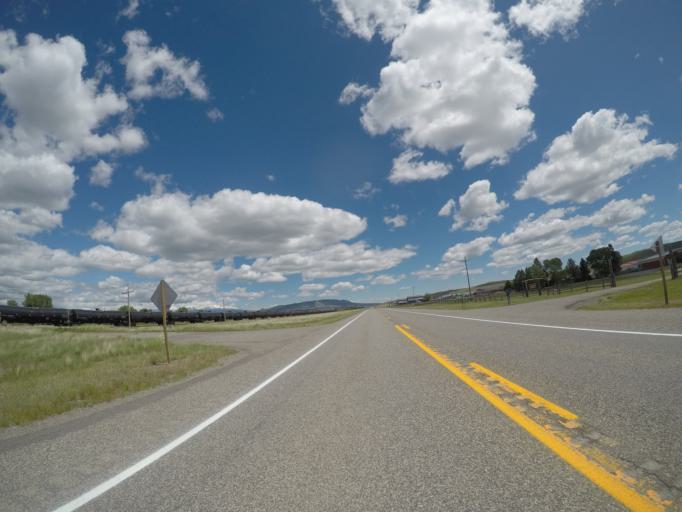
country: US
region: Montana
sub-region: Park County
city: Livingston
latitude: 45.6821
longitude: -110.5184
